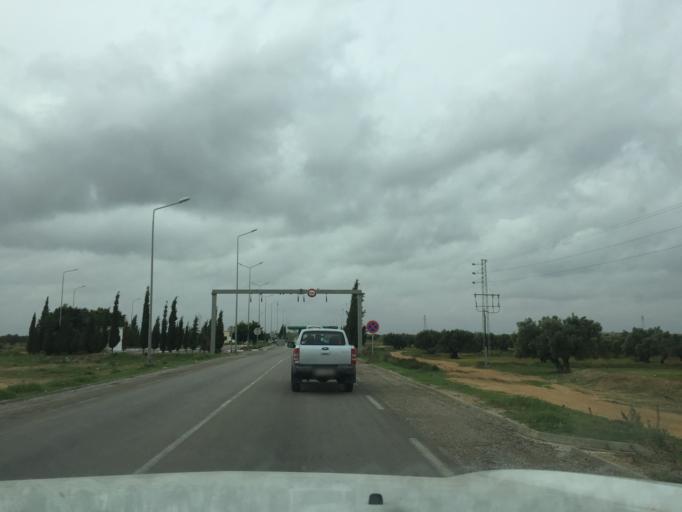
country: TN
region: Susah
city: Masakin
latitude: 35.6464
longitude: 10.5849
